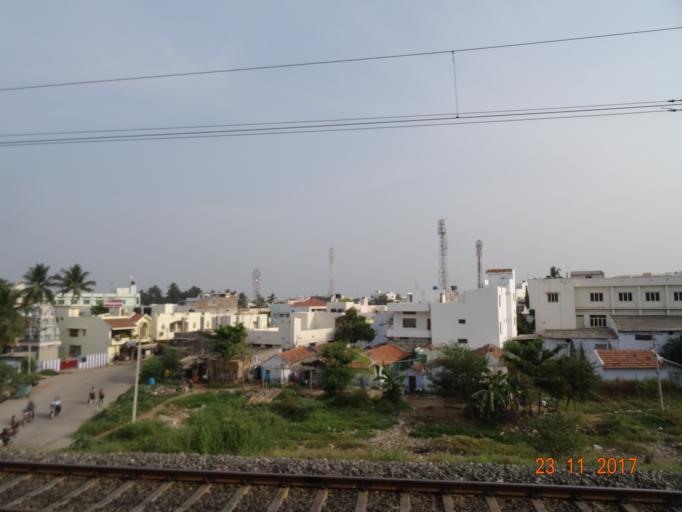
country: IN
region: Tamil Nadu
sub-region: Tiruppur
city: Tiruppur
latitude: 11.1153
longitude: 77.3611
